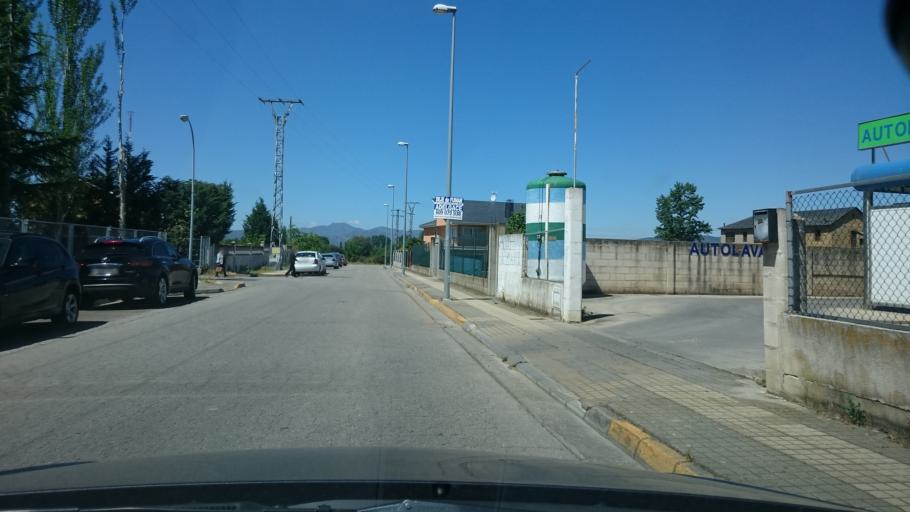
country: ES
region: Castille and Leon
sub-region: Provincia de Leon
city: Camponaraya
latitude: 42.5739
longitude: -6.6442
